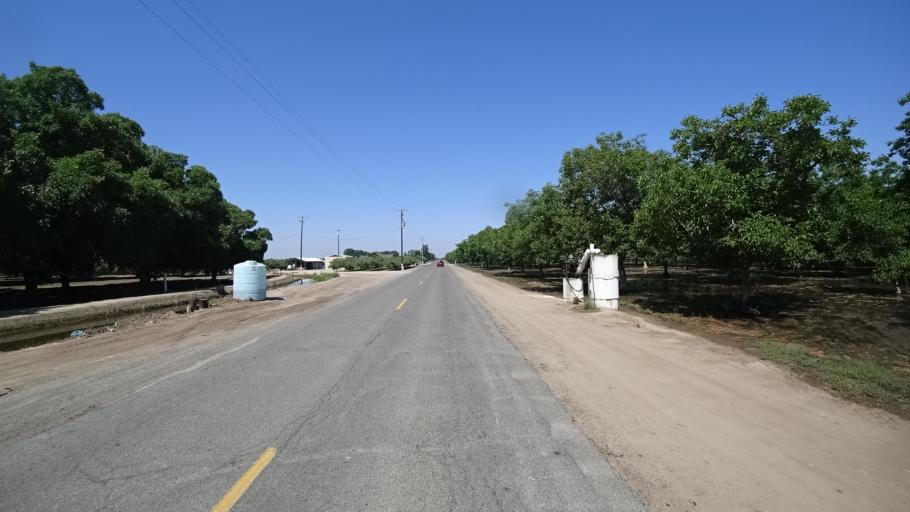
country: US
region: California
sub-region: Kings County
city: Lucerne
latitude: 36.3717
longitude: -119.6755
